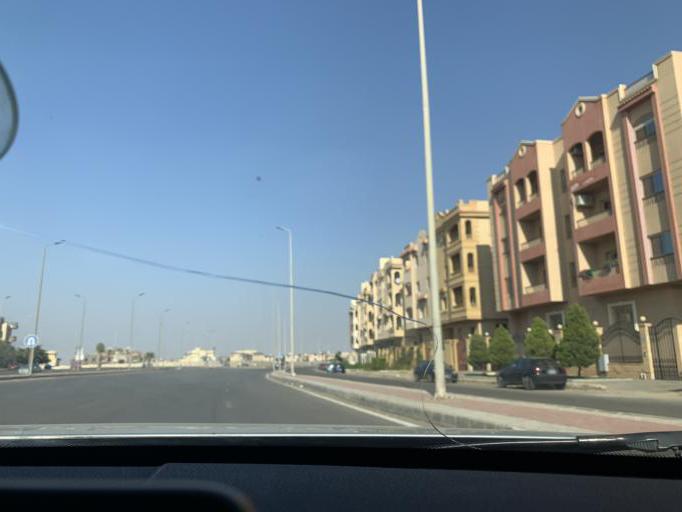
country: EG
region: Muhafazat al Qahirah
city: Cairo
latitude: 30.0051
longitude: 31.4694
